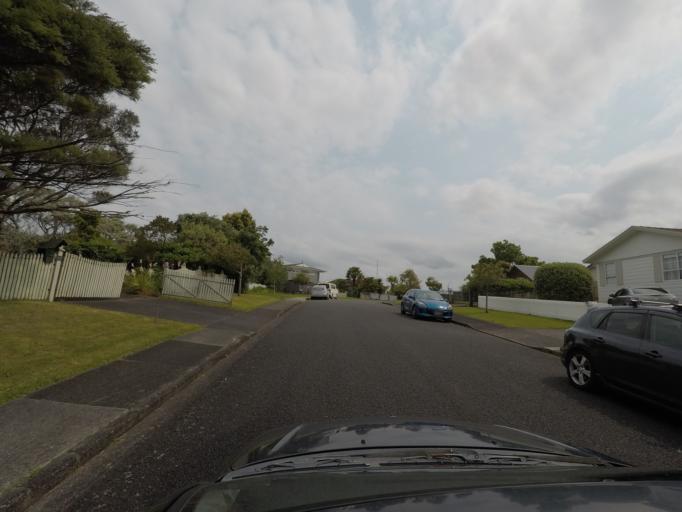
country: NZ
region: Auckland
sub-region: Auckland
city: Rosebank
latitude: -36.8415
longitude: 174.6370
